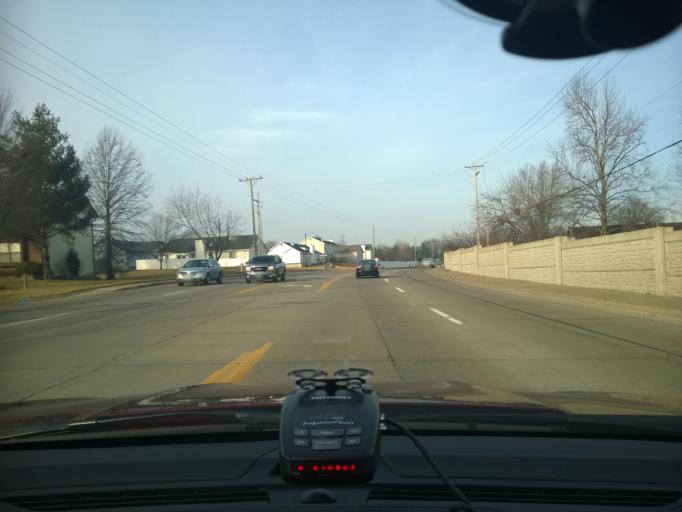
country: US
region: Missouri
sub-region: Saint Charles County
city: Saint Peters
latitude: 38.7869
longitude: -90.6482
